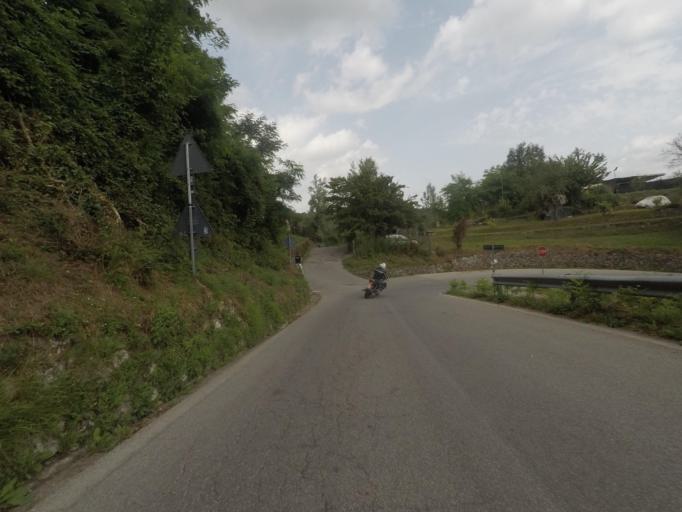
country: IT
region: Tuscany
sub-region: Provincia di Lucca
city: Castelnuovo di Garfagnana
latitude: 44.1109
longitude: 10.3748
